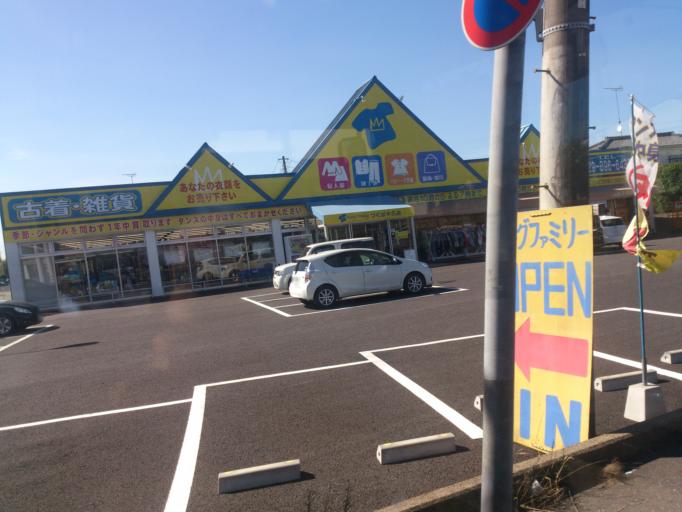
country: JP
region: Ibaraki
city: Ushiku
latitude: 35.9884
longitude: 140.1415
